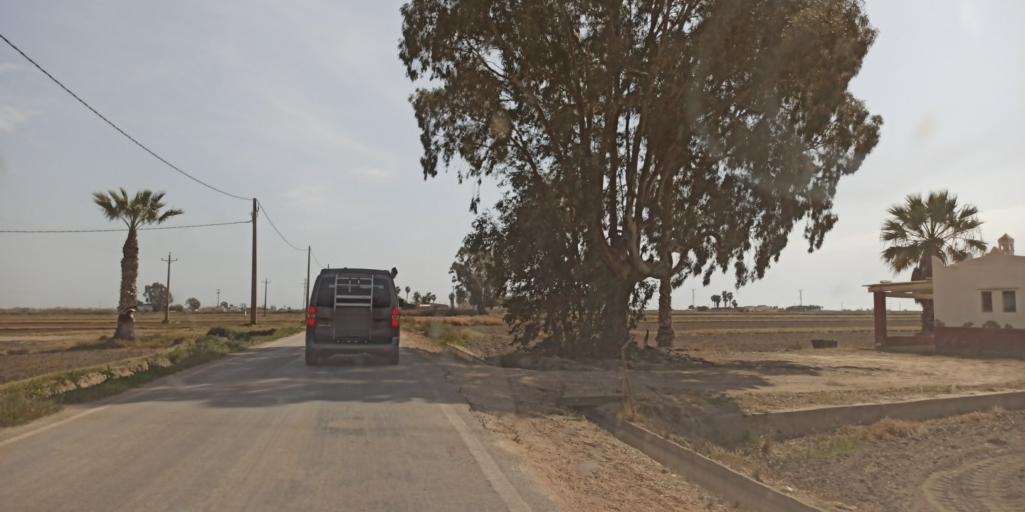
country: ES
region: Catalonia
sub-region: Provincia de Tarragona
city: Deltebre
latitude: 40.6464
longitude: 0.7129
